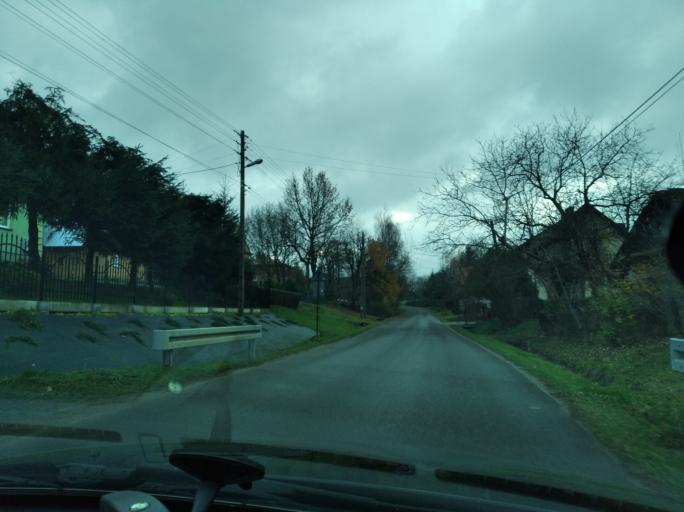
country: PL
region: Subcarpathian Voivodeship
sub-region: Powiat przeworski
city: Sietesz
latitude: 49.9886
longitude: 22.3491
